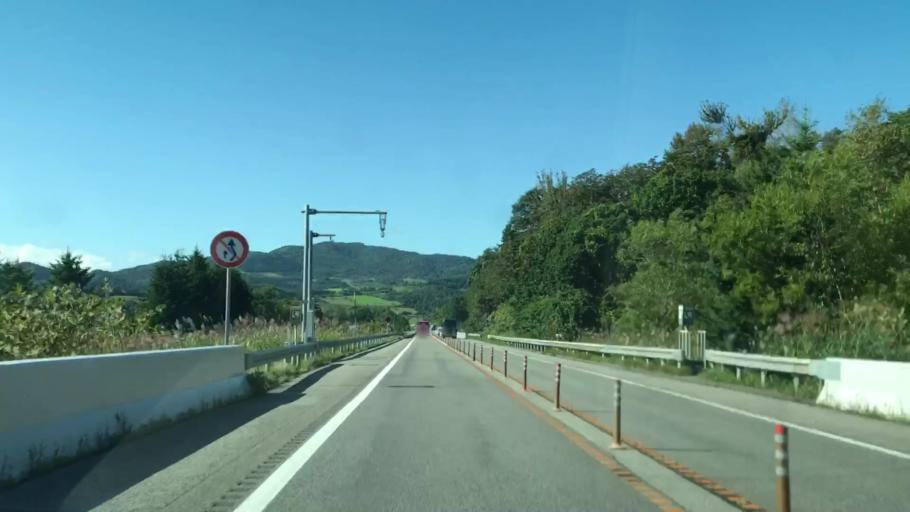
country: JP
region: Hokkaido
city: Date
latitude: 42.5354
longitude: 140.7979
